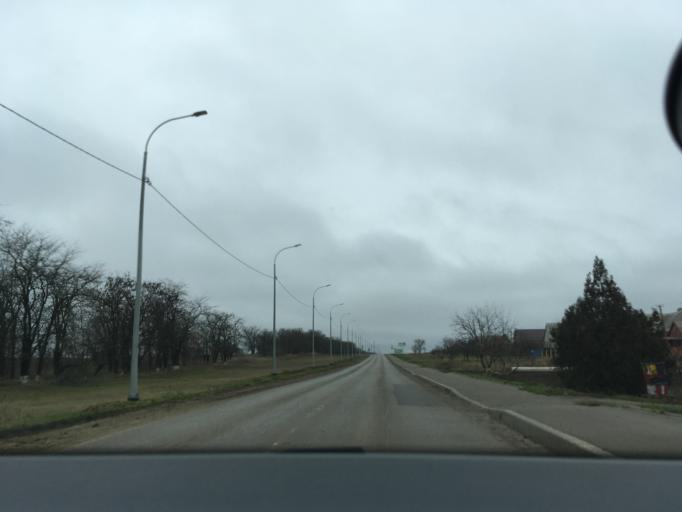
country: RU
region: Krasnodarskiy
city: Kushchevskaya
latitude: 46.5808
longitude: 39.6387
